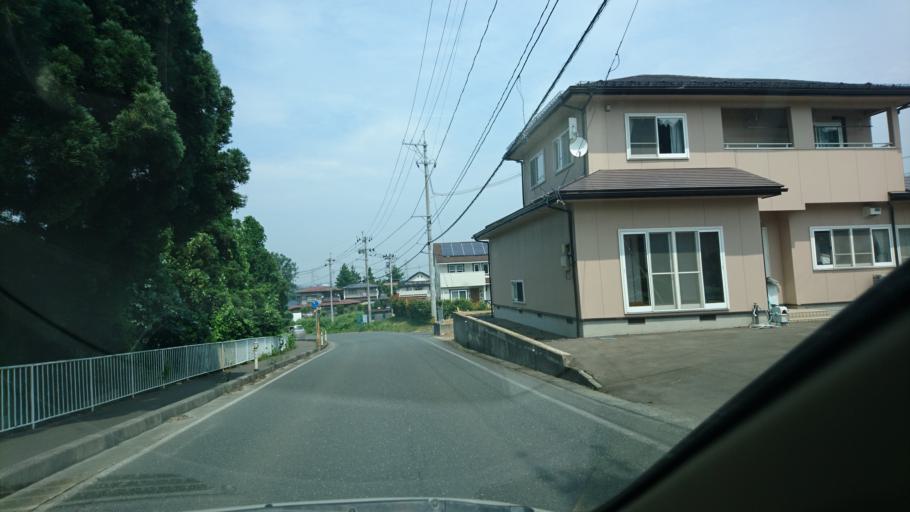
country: JP
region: Iwate
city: Kitakami
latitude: 39.2680
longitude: 141.0915
